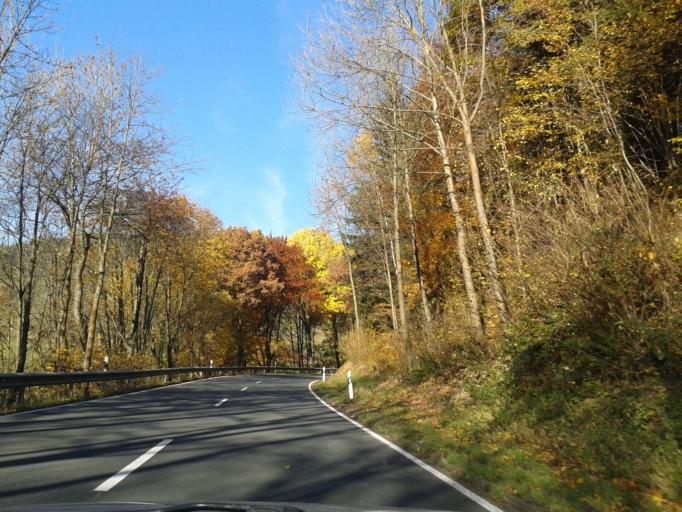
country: DE
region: North Rhine-Westphalia
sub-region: Regierungsbezirk Arnsberg
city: Bad Laasphe
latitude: 50.9629
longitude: 8.3481
